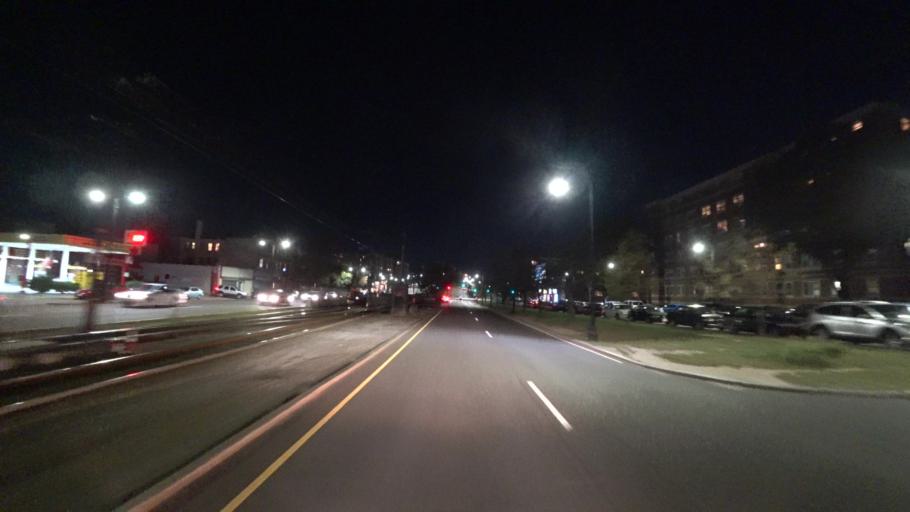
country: US
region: Massachusetts
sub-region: Norfolk County
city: Brookline
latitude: 42.3450
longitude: -71.1421
